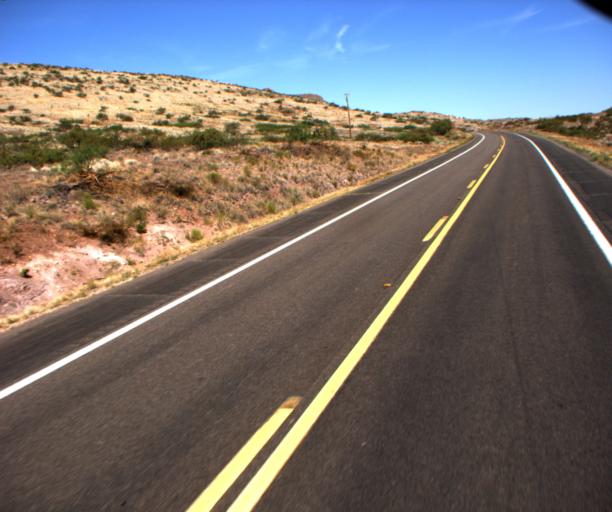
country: US
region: Arizona
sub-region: Greenlee County
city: Clifton
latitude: 32.7484
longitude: -109.2288
